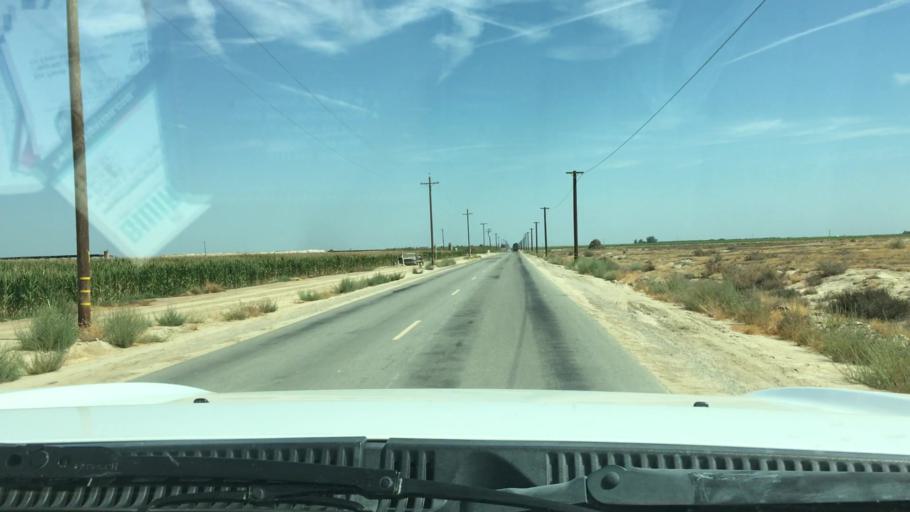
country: US
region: California
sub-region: Kern County
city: Shafter
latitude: 35.4457
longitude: -119.3681
